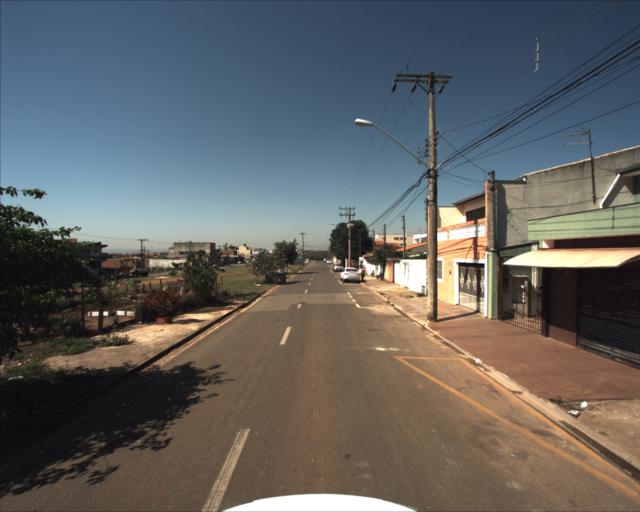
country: BR
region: Sao Paulo
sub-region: Sorocaba
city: Sorocaba
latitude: -23.4952
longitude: -47.5309
